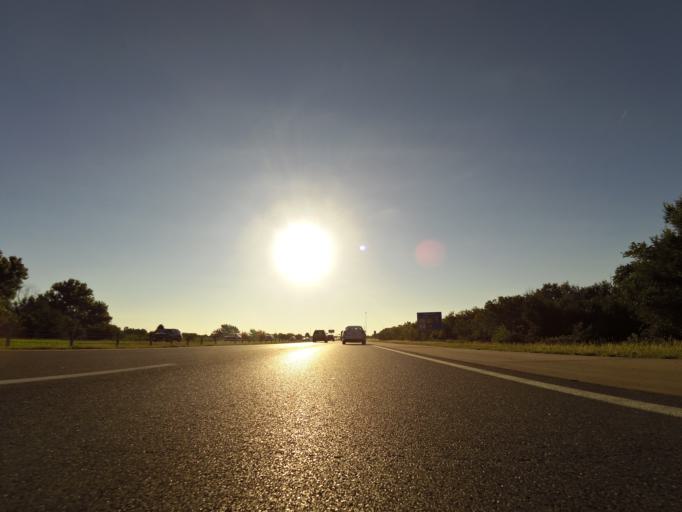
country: US
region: Kansas
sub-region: Sedgwick County
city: Bellaire
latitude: 37.7454
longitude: -97.2712
